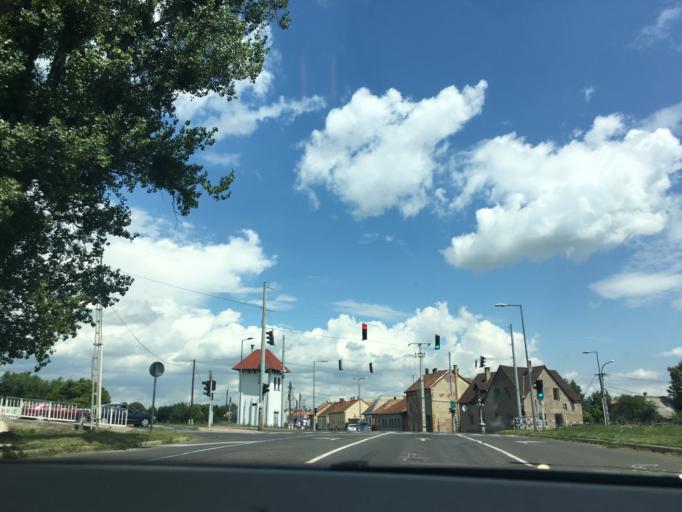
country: HU
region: Borsod-Abauj-Zemplen
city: Satoraljaujhely
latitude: 48.3996
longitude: 21.6620
